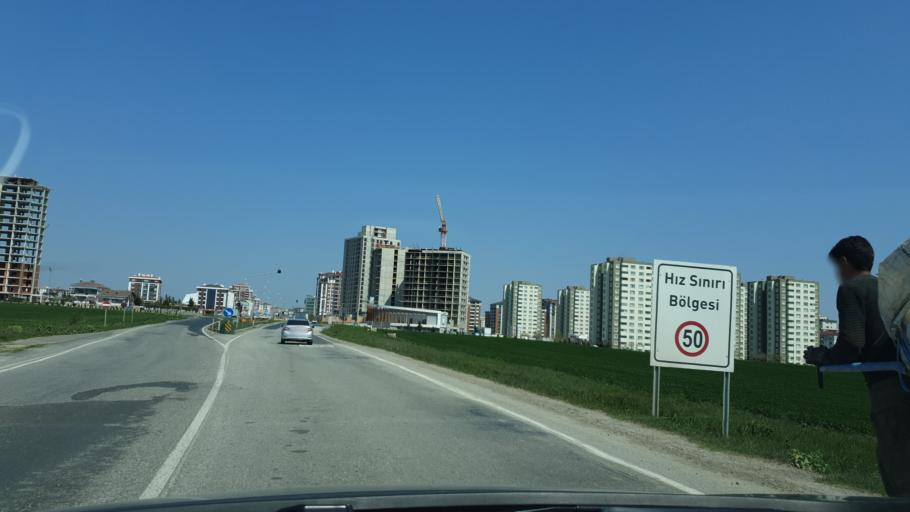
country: TR
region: Tekirdag
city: Corlu
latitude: 41.1478
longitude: 27.7749
